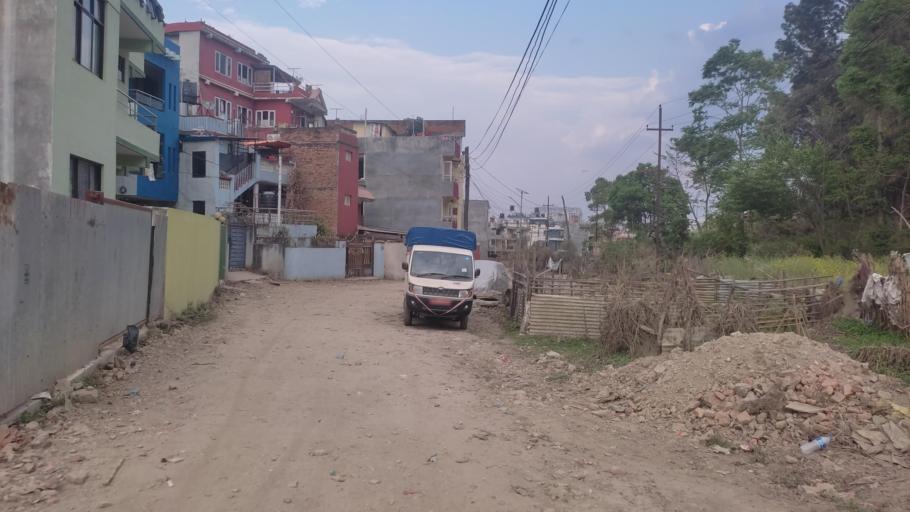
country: NP
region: Central Region
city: Kirtipur
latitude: 27.6811
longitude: 85.2930
